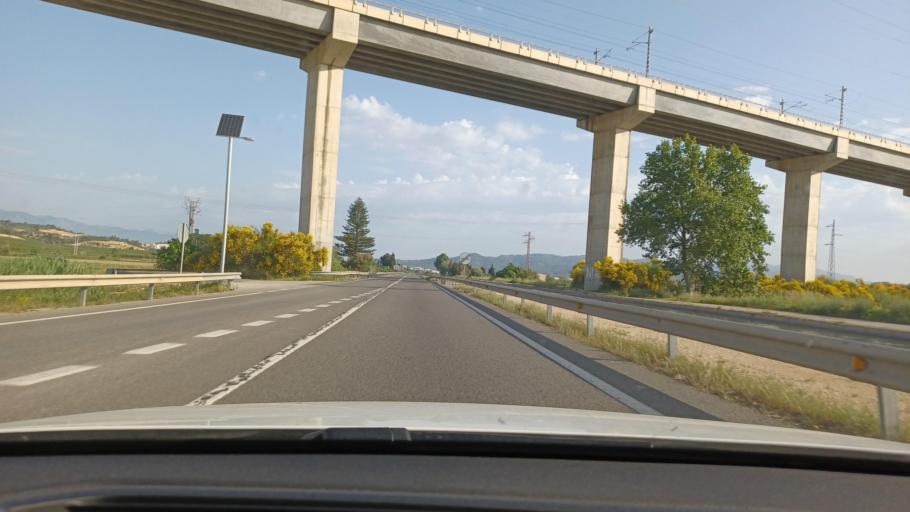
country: ES
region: Catalonia
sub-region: Provincia de Tarragona
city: Amposta
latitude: 40.7281
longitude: 0.5711
